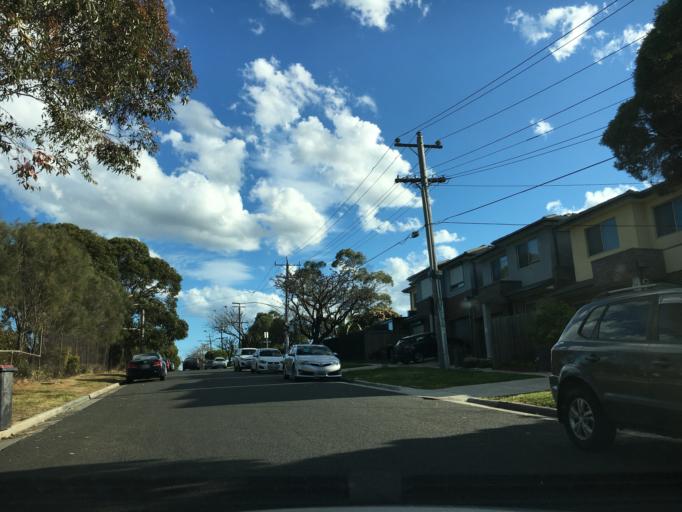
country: AU
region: Victoria
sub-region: Monash
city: Chadstone
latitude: -37.8980
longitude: 145.1107
